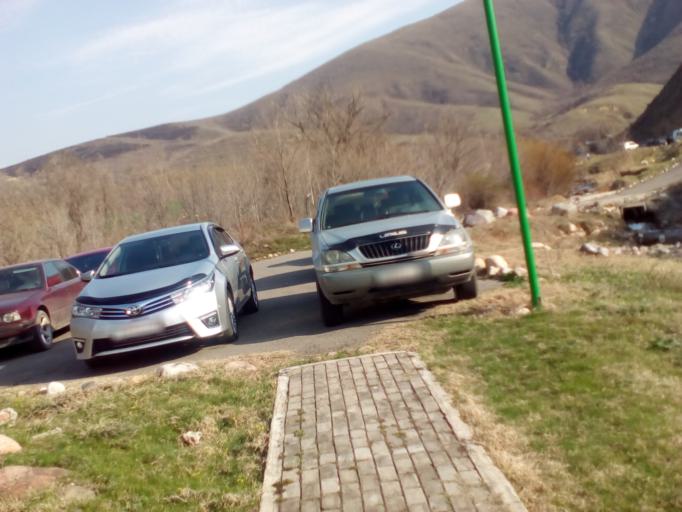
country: KZ
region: Almaty Oblysy
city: Burunday
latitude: 43.1523
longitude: 76.5708
